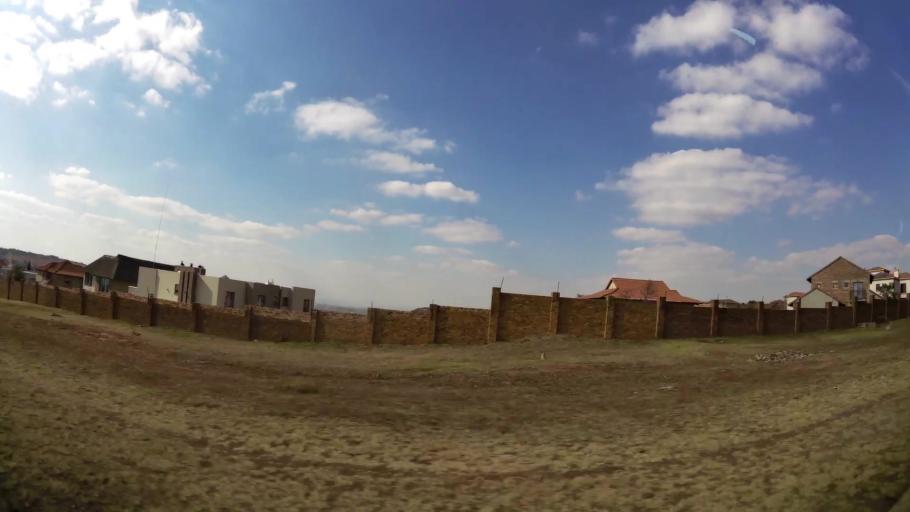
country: ZA
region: Gauteng
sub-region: West Rand District Municipality
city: Krugersdorp
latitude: -26.0568
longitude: 27.7548
